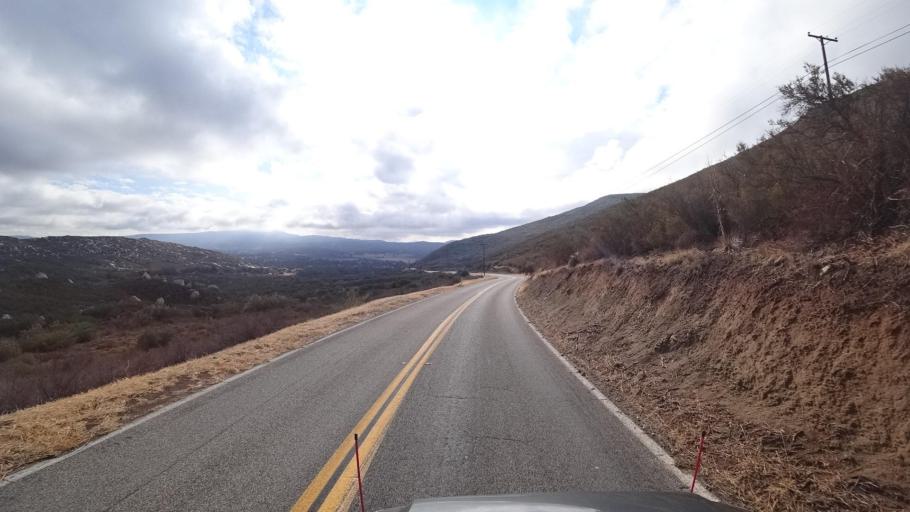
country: MX
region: Baja California
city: Tecate
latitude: 32.6284
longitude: -116.6323
